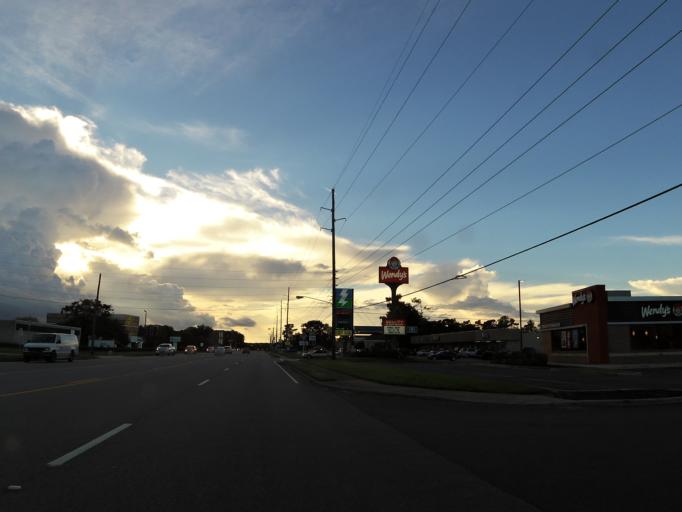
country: US
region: Georgia
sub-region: Camden County
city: St Marys
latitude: 30.7500
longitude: -81.5718
